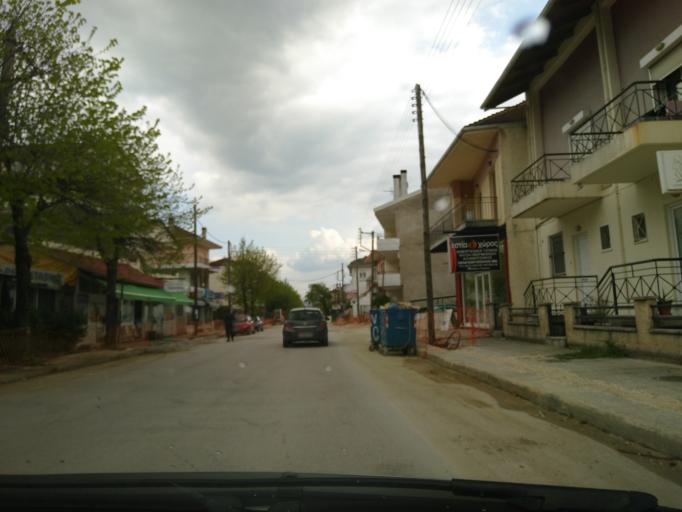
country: GR
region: Epirus
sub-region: Nomos Ioanninon
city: Anatoli
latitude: 39.6472
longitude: 20.8620
